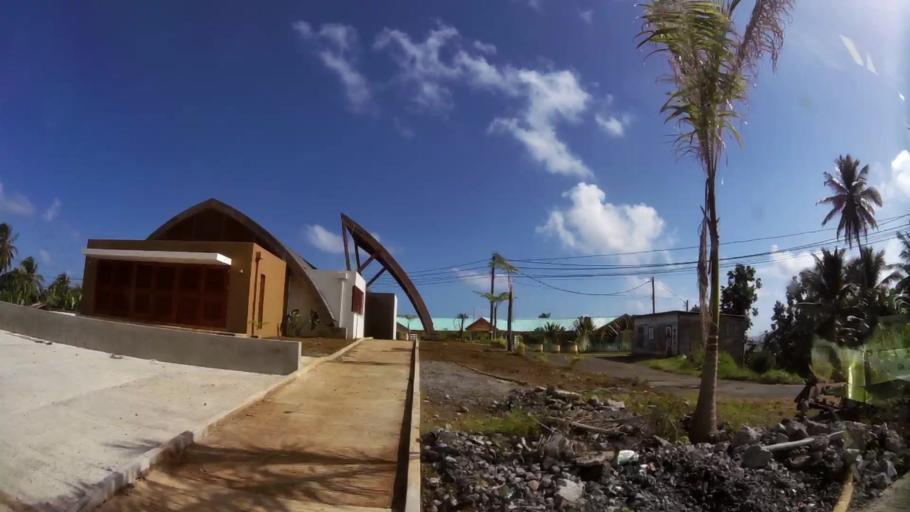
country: DM
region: Saint David
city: Castle Bruce
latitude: 15.4899
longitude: -61.2532
